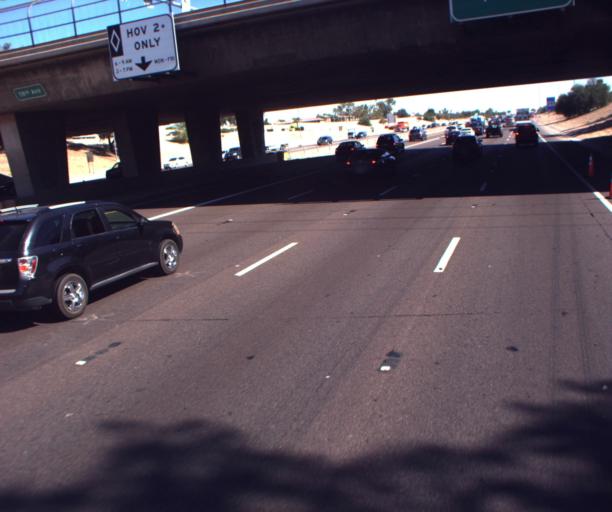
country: US
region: Arizona
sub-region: Maricopa County
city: Tolleson
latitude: 33.4627
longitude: -112.1869
